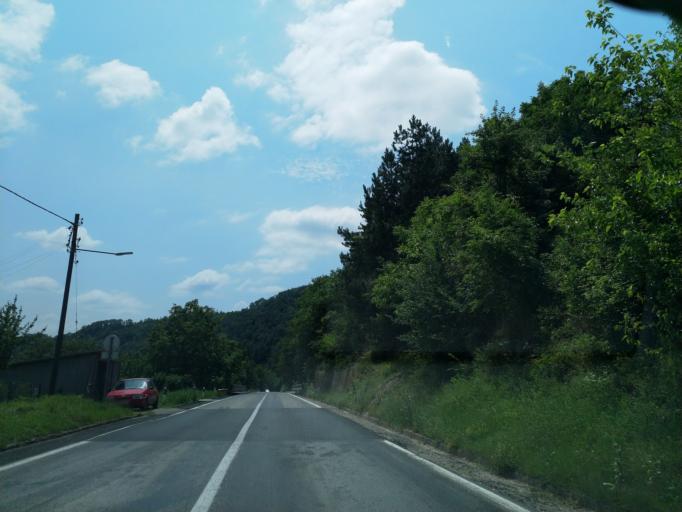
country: RS
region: Central Serbia
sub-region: Rasinski Okrug
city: Aleksandrovac
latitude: 43.4112
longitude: 21.1563
